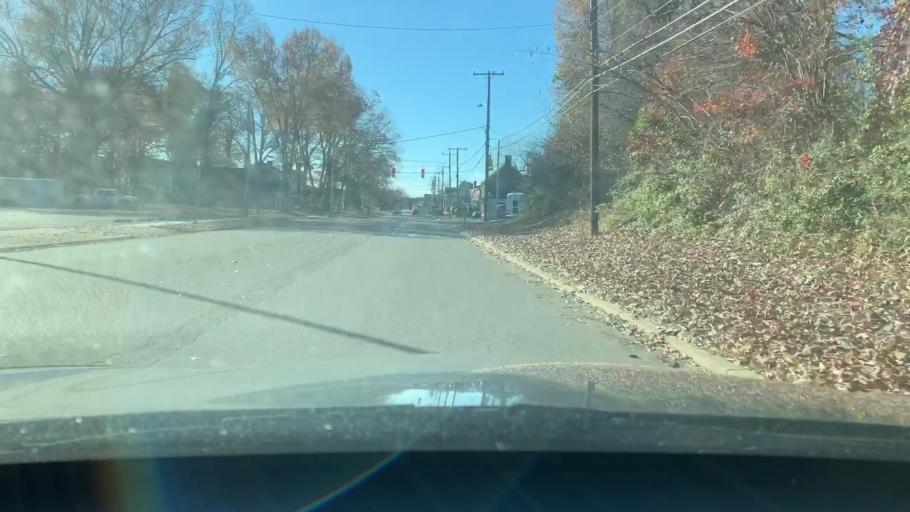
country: US
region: North Carolina
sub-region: Alamance County
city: Burlington
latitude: 36.0928
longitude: -79.4292
